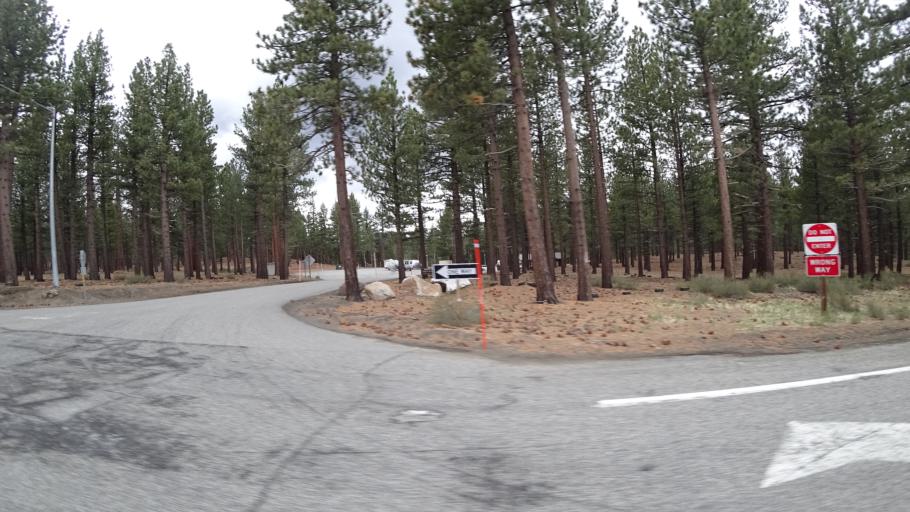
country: US
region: California
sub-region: Mono County
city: Mammoth Lakes
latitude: 37.7317
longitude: -118.9682
